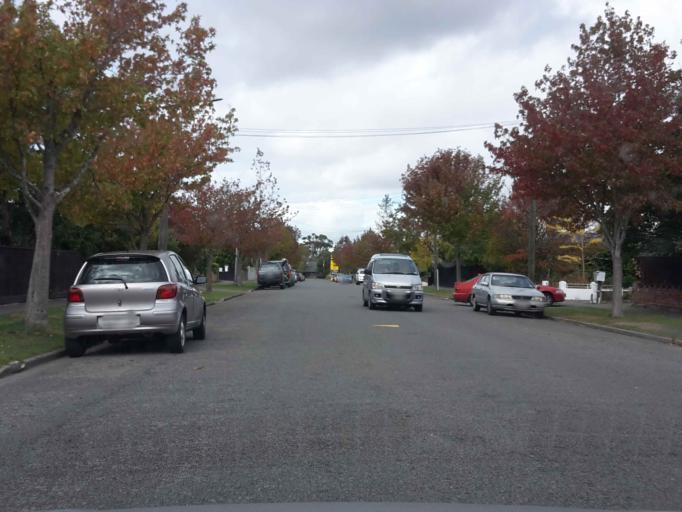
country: NZ
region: Canterbury
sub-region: Christchurch City
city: Christchurch
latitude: -43.4894
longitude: 172.6154
